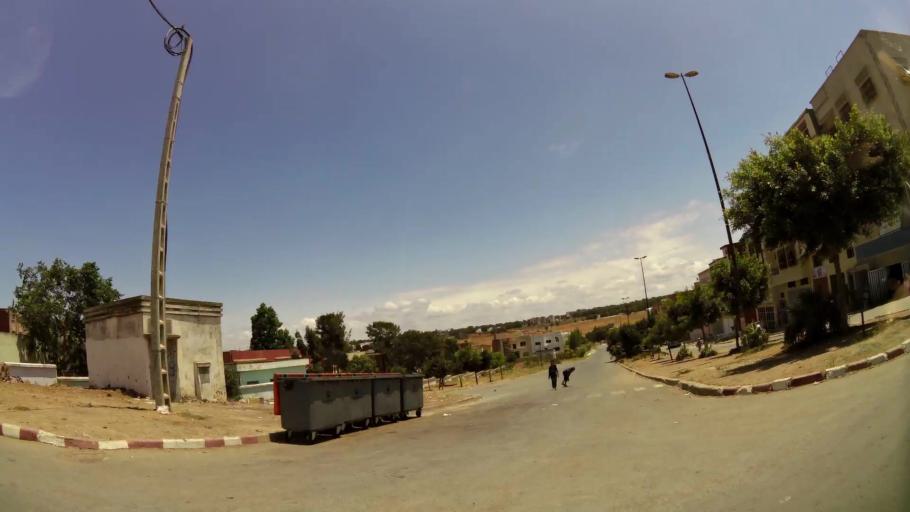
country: MA
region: Gharb-Chrarda-Beni Hssen
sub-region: Kenitra Province
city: Kenitra
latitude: 34.2641
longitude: -6.6435
